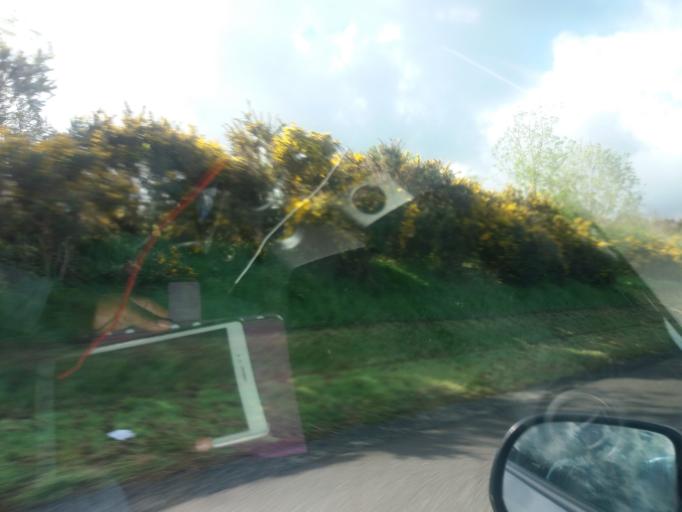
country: IE
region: Leinster
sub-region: Loch Garman
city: Gorey
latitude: 52.6419
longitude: -6.3376
